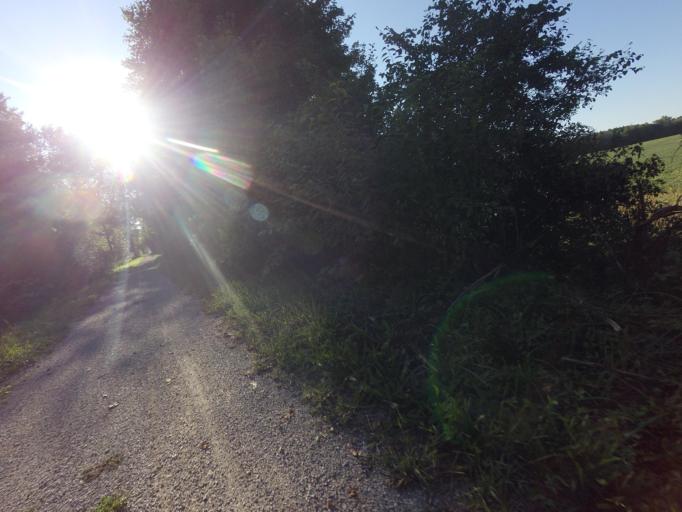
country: CA
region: Ontario
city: Goderich
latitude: 43.7529
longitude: -81.6119
